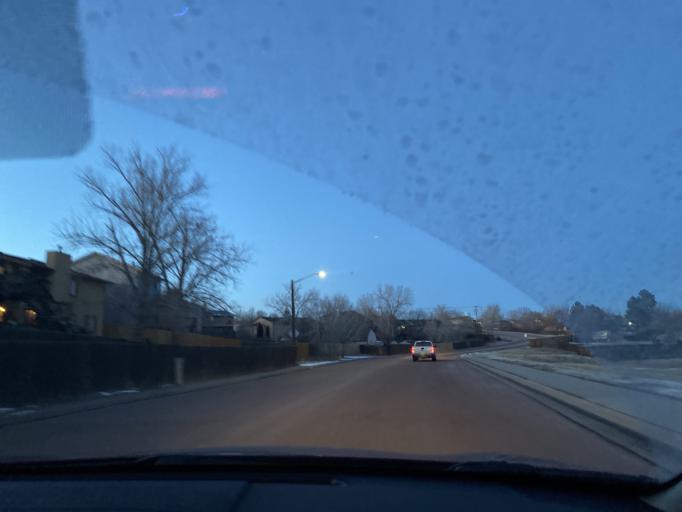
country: US
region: Colorado
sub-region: El Paso County
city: Security-Widefield
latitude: 38.7203
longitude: -104.6902
